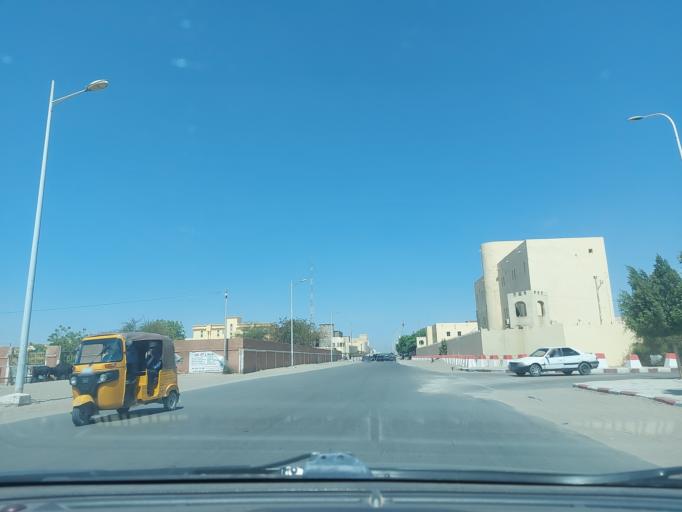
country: MR
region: Nouakchott
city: Nouakchott
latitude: 18.0808
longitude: -15.9726
